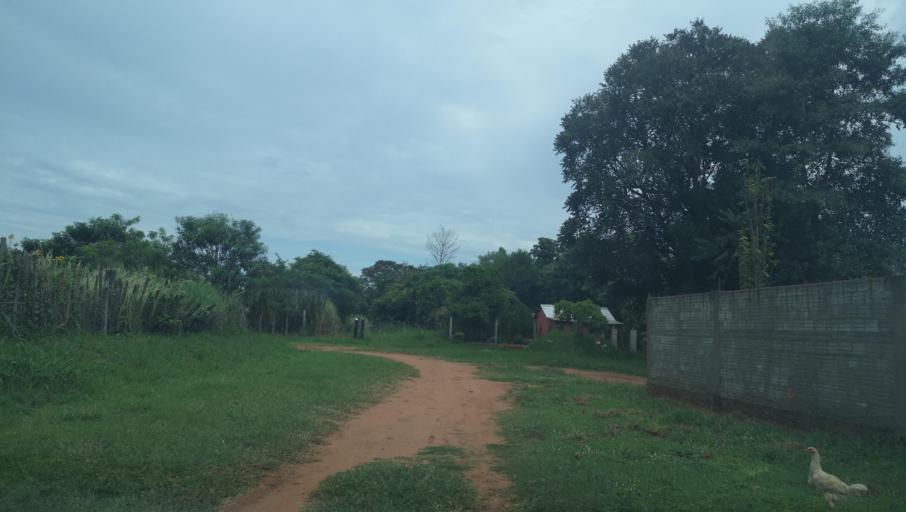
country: PY
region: San Pedro
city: Capiibary
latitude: -24.7433
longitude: -56.0267
